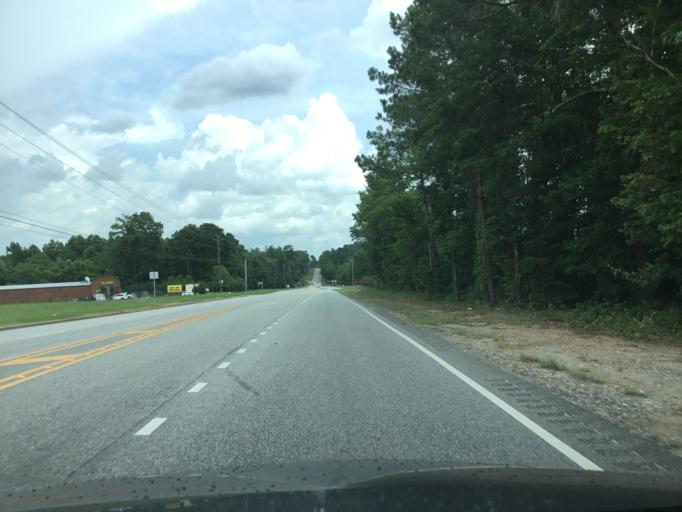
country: US
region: Alabama
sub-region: Montgomery County
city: Pike Road
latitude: 32.3468
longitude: -86.0891
